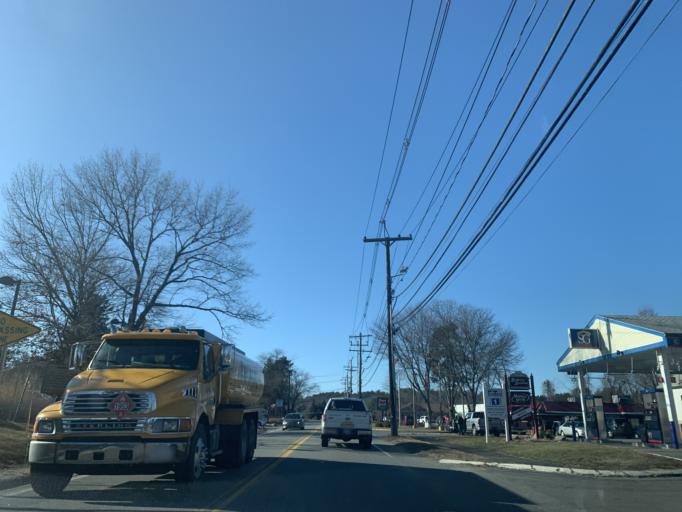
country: US
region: Massachusetts
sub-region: Middlesex County
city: Wayland
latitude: 42.3631
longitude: -71.3922
